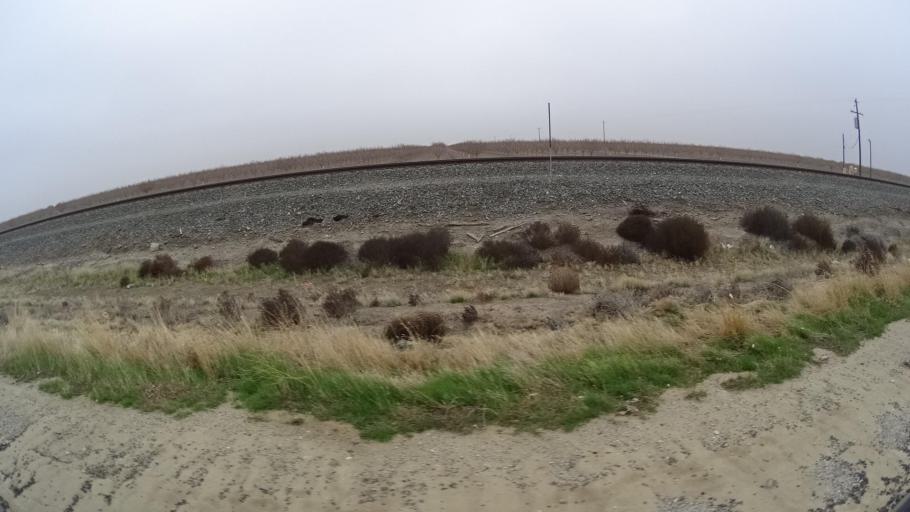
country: US
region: California
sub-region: Kern County
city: Greenfield
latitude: 35.1801
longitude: -119.1721
